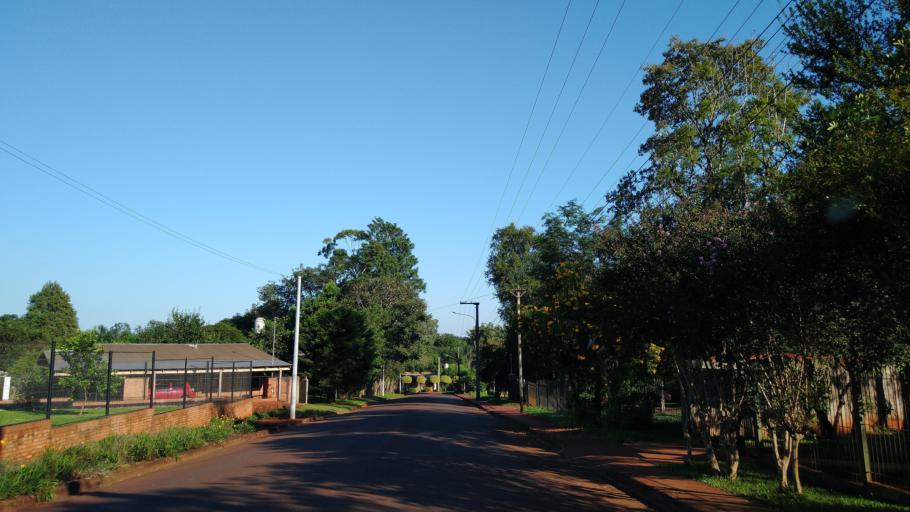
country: AR
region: Misiones
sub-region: Departamento de Montecarlo
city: Montecarlo
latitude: -26.5656
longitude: -54.7509
